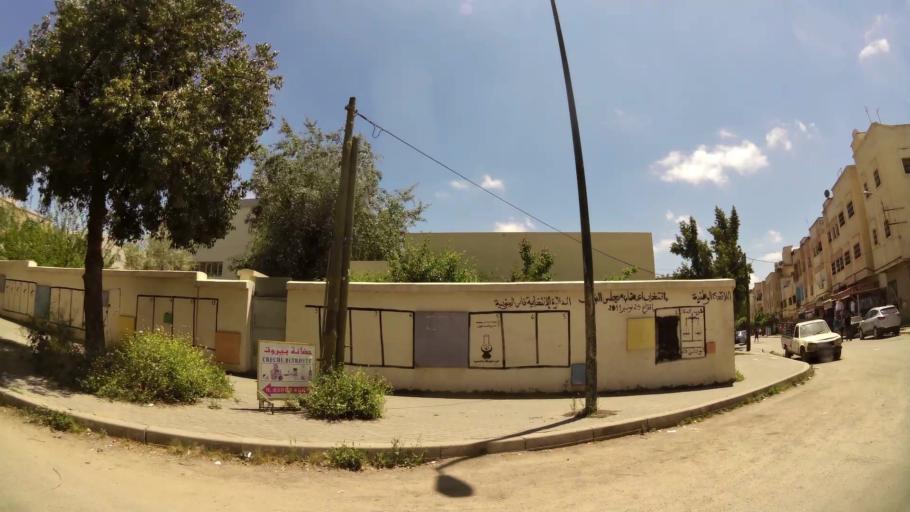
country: MA
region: Fes-Boulemane
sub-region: Fes
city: Fes
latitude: 34.0077
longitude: -4.9841
